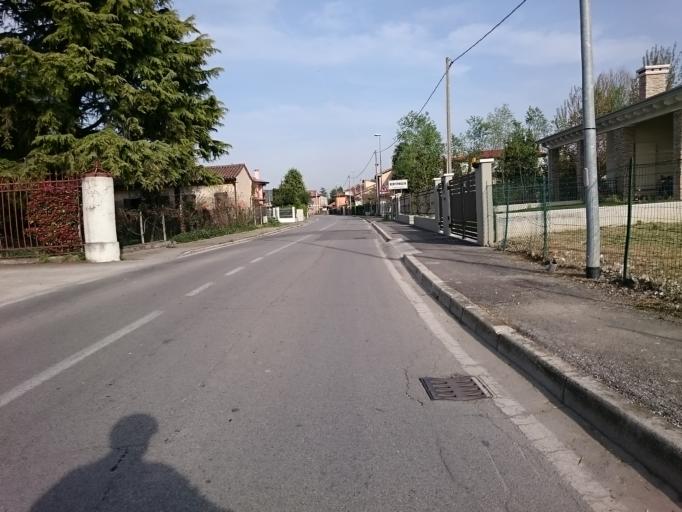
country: IT
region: Veneto
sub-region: Provincia di Padova
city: Bertipaglia
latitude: 45.3126
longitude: 11.8798
